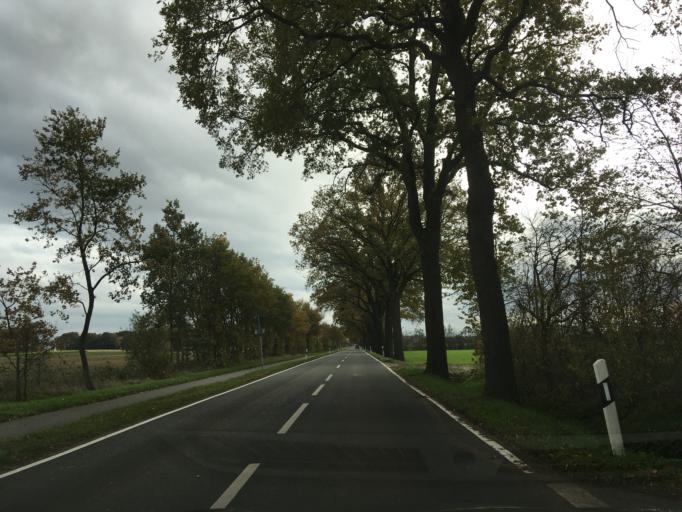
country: DE
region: North Rhine-Westphalia
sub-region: Regierungsbezirk Munster
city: Vreden
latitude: 52.0979
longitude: 6.8848
